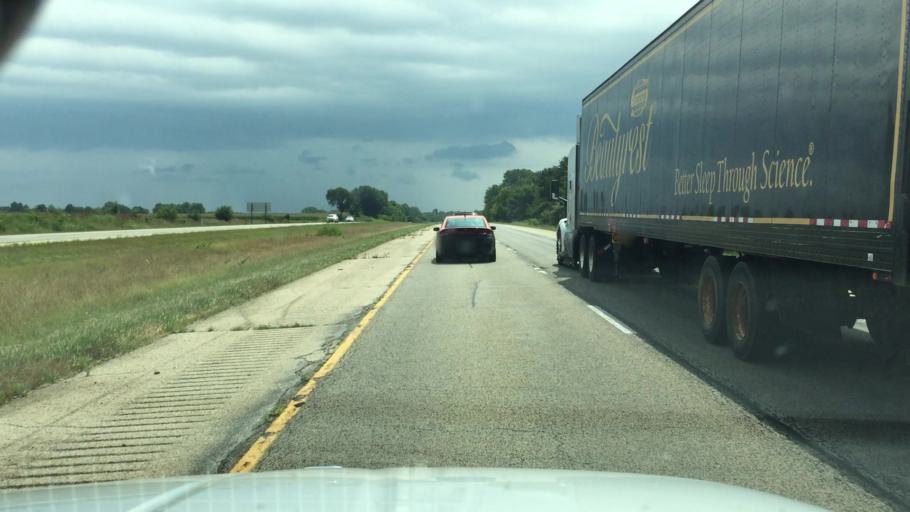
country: US
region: Illinois
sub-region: Peoria County
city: Elmwood
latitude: 40.8157
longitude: -89.8493
